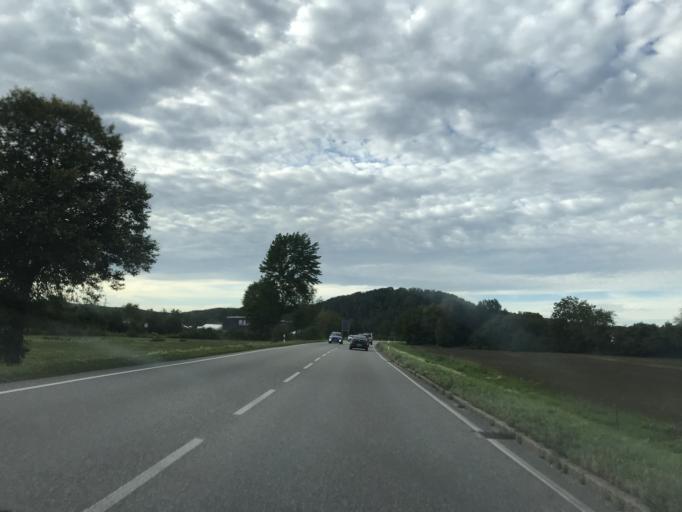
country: CH
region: Aargau
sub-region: Bezirk Rheinfelden
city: Mumpf
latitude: 47.5769
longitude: 7.9130
